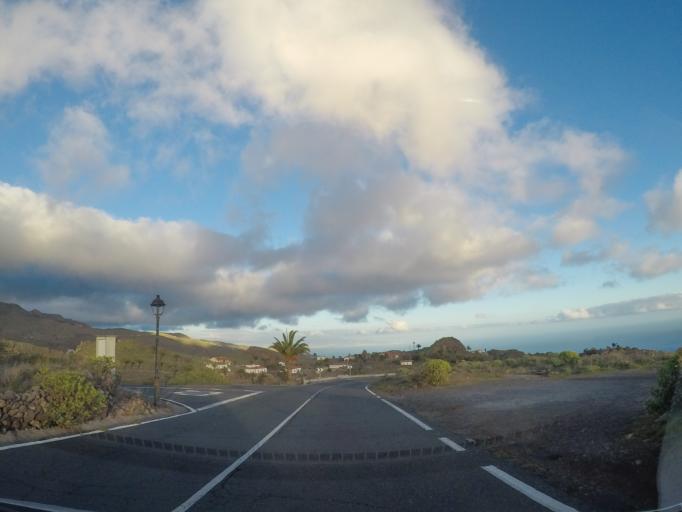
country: ES
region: Canary Islands
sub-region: Provincia de Santa Cruz de Tenerife
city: Alajero
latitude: 28.0573
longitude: -17.2284
